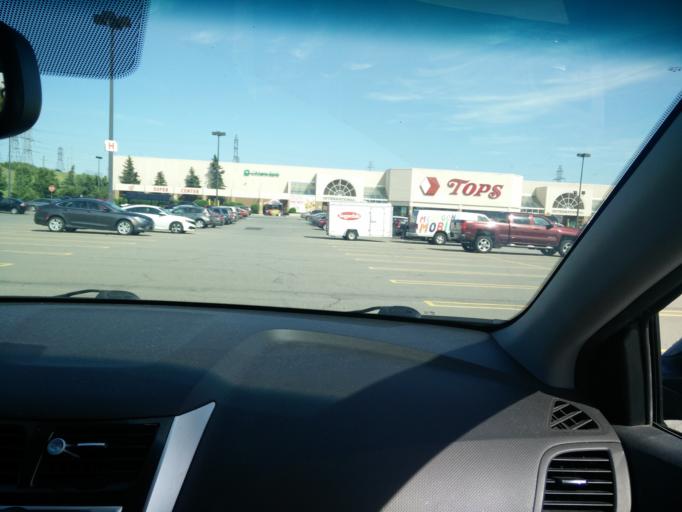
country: US
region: New York
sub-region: Erie County
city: West Seneca
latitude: 42.8336
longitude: -78.7855
